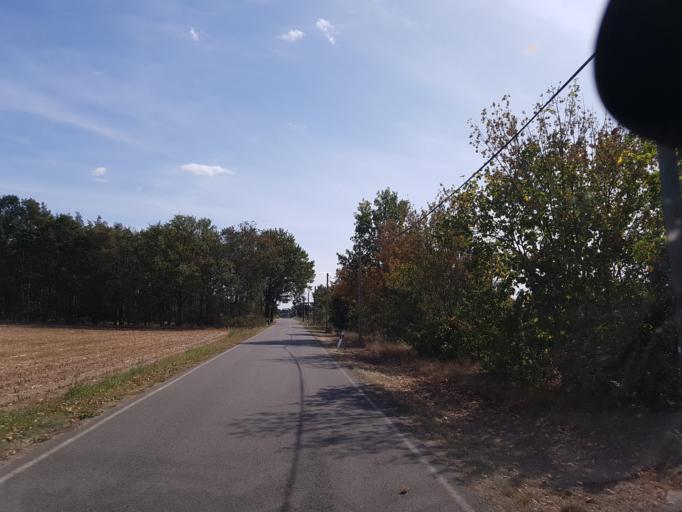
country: DE
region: Brandenburg
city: Luckau
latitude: 51.8583
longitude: 13.6550
